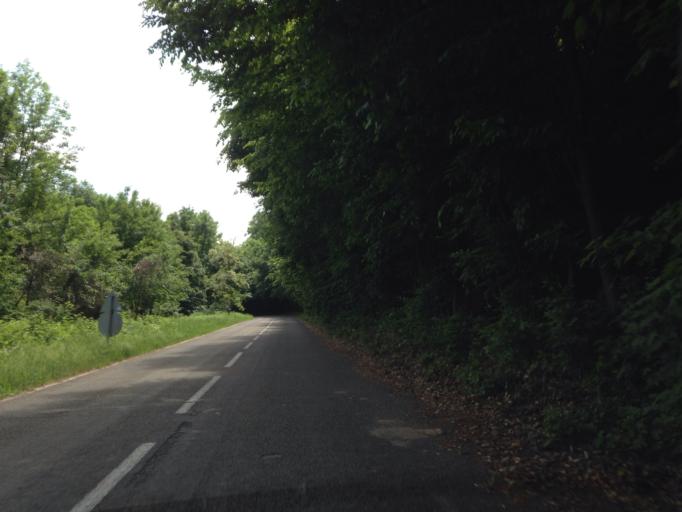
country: HU
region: Pest
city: Visegrad
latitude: 47.7341
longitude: 18.9553
